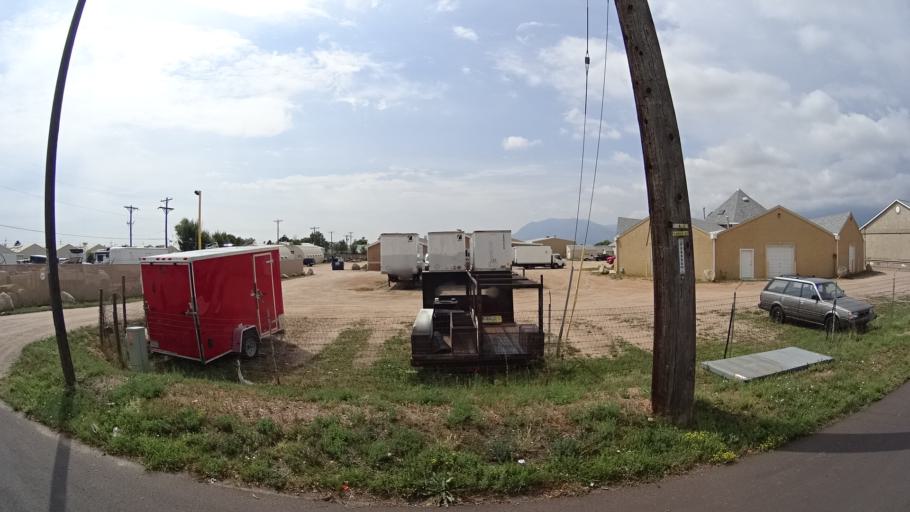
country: US
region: Colorado
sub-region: El Paso County
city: Colorado Springs
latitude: 38.8789
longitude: -104.8210
